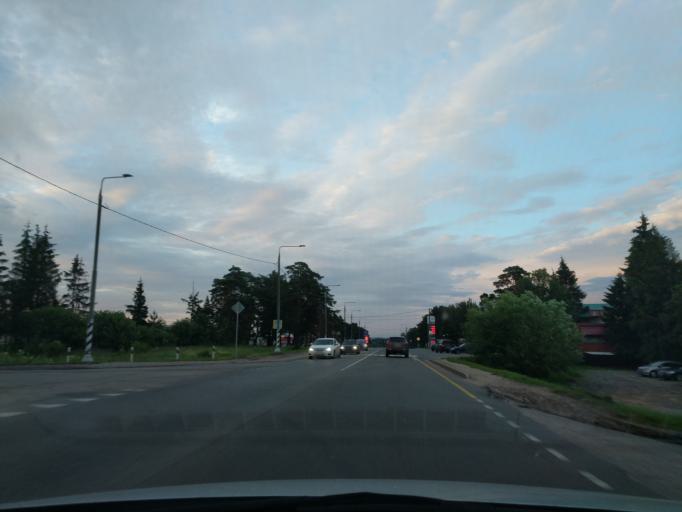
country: RU
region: Kaluga
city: Maloyaroslavets
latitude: 55.0199
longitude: 36.4977
